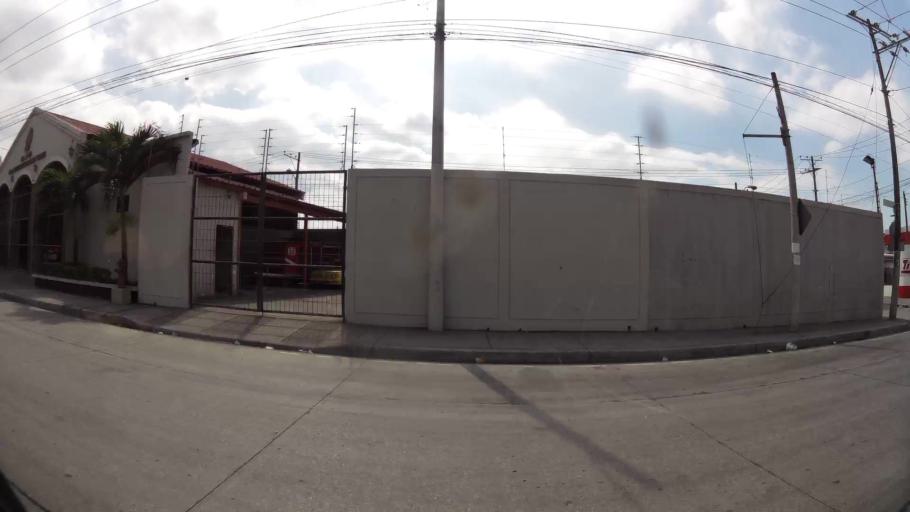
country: EC
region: Guayas
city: Eloy Alfaro
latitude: -2.0852
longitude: -79.9209
